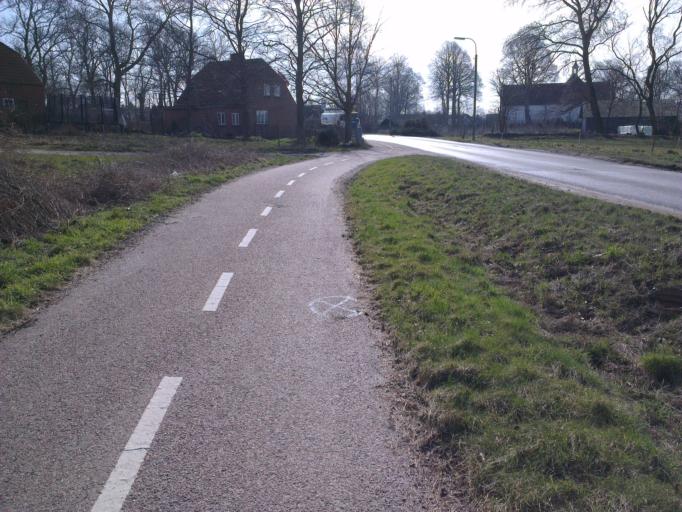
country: DK
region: Capital Region
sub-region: Frederikssund Kommune
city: Skibby
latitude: 55.7958
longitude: 11.9152
